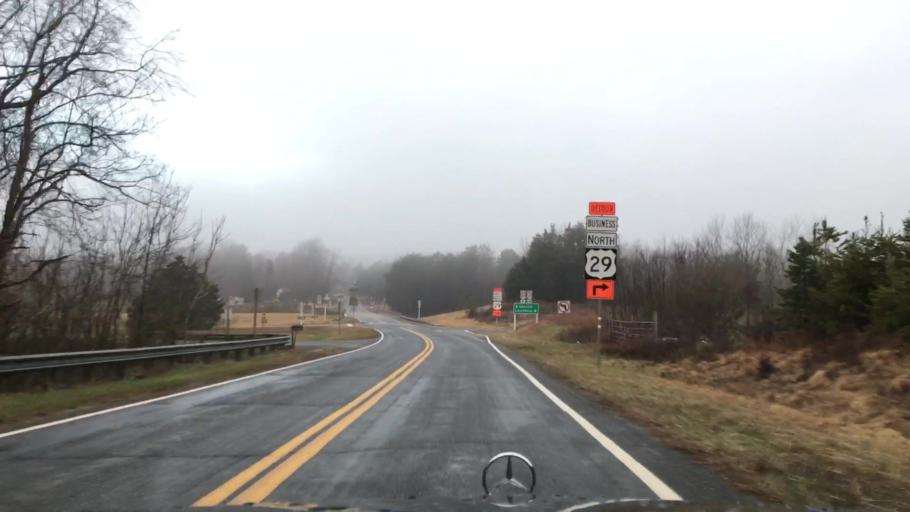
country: US
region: Virginia
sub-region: Pittsylvania County
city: Hurt
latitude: 37.1144
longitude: -79.3242
